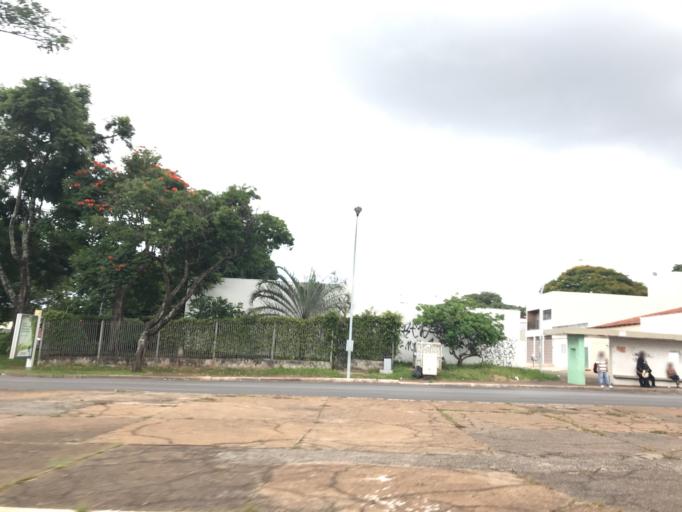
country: BR
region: Federal District
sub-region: Brasilia
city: Brasilia
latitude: -15.8159
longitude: -47.9110
